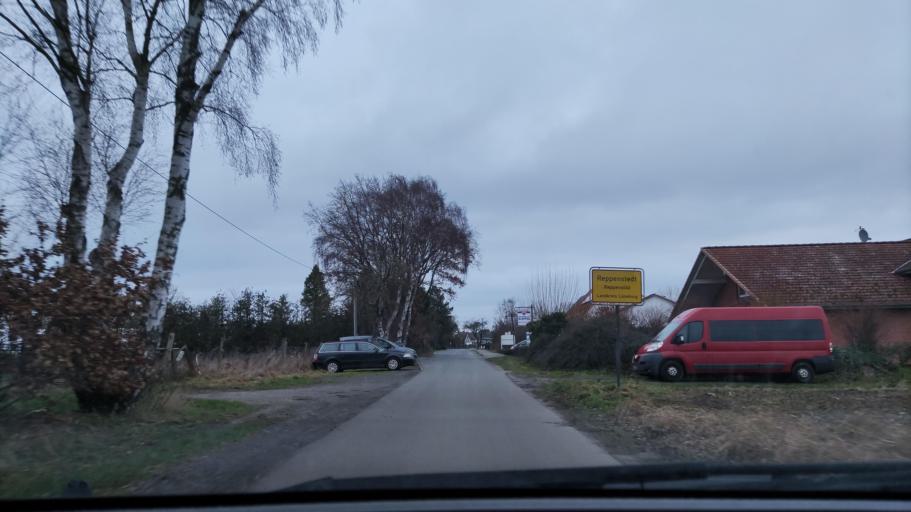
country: DE
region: Lower Saxony
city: Reppenstedt
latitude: 53.2434
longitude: 10.3501
